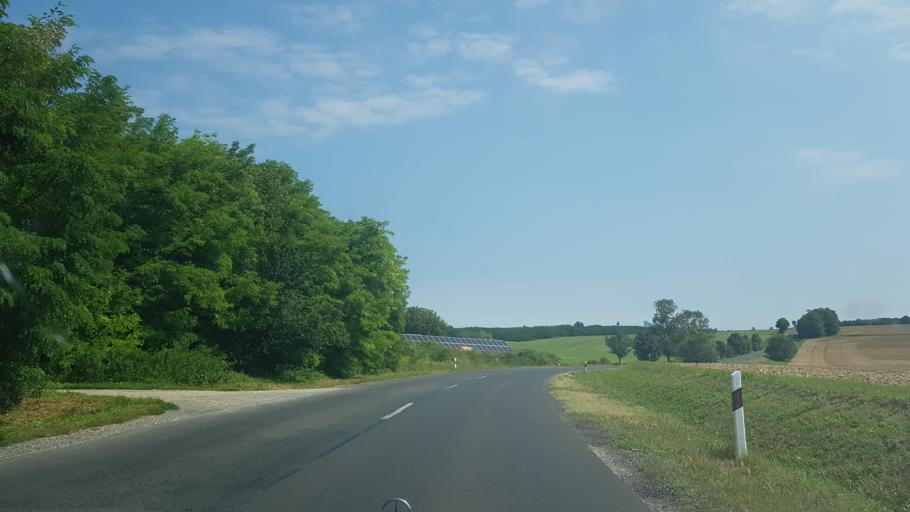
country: HU
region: Somogy
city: Bohonye
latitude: 46.4655
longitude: 17.3747
